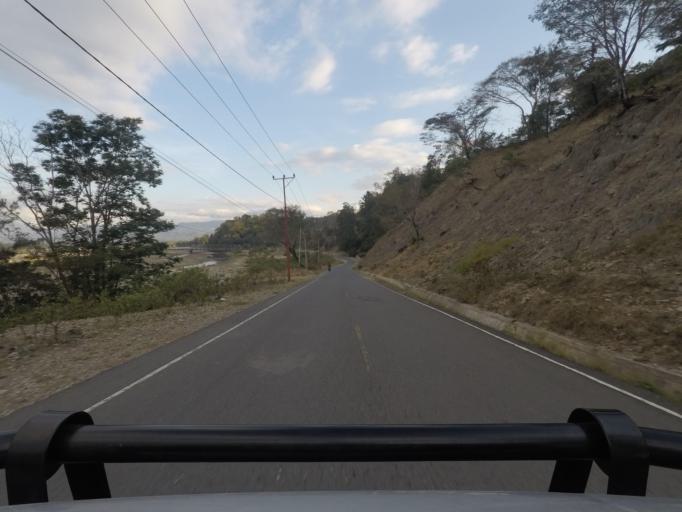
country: TL
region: Bobonaro
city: Maliana
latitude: -8.9566
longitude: 125.1092
